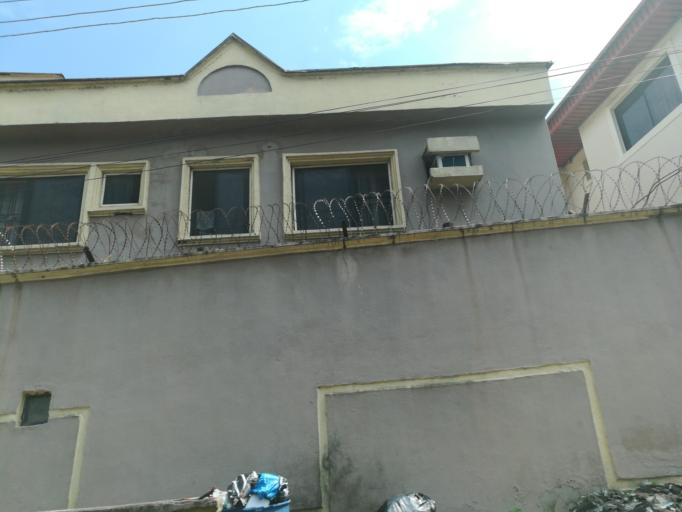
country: NG
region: Lagos
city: Oshodi
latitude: 6.5449
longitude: 3.3221
